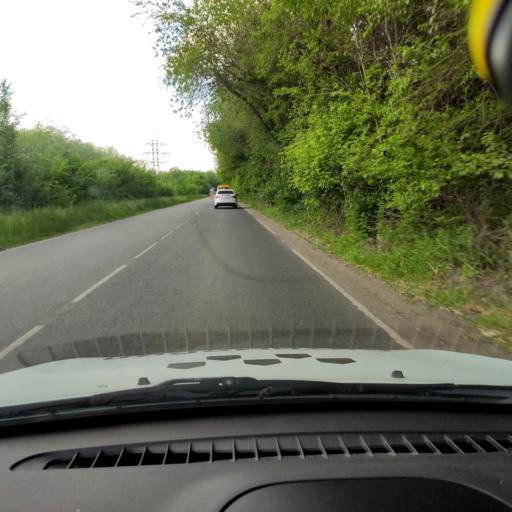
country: RU
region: Samara
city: Tol'yatti
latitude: 53.5792
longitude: 49.2558
